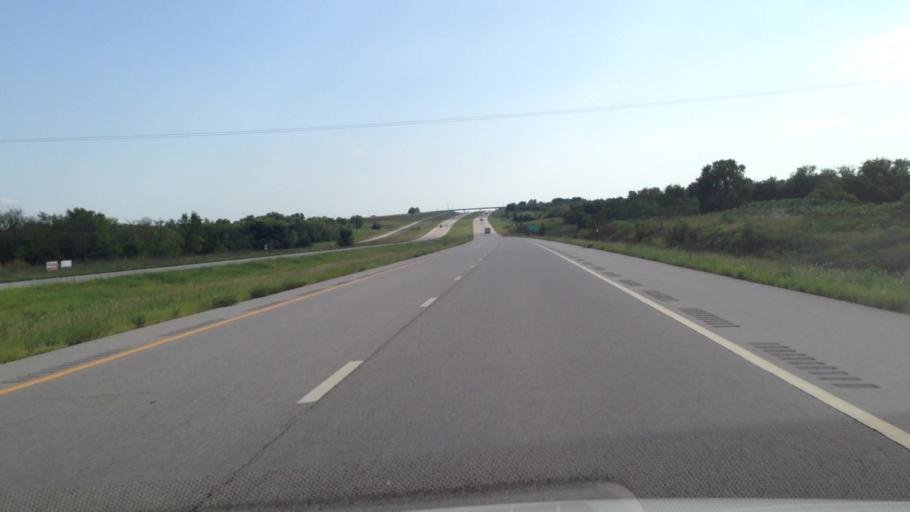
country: US
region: Kansas
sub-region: Linn County
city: La Cygne
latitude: 38.4186
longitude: -94.6878
